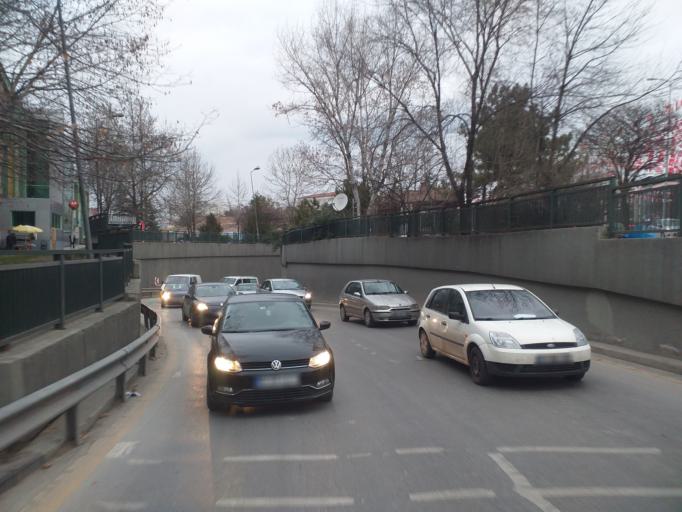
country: TR
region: Ankara
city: Ankara
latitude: 39.9573
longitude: 32.8177
